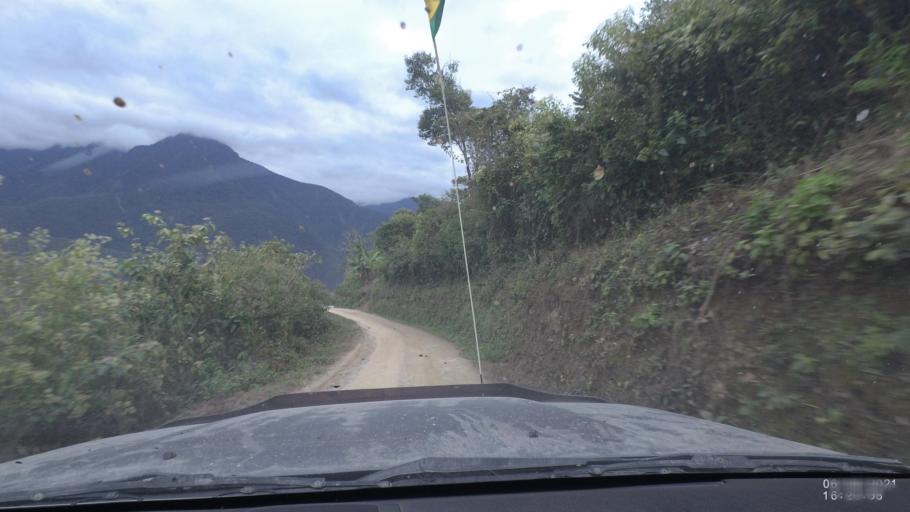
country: BO
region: La Paz
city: Quime
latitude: -16.5409
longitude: -66.7544
